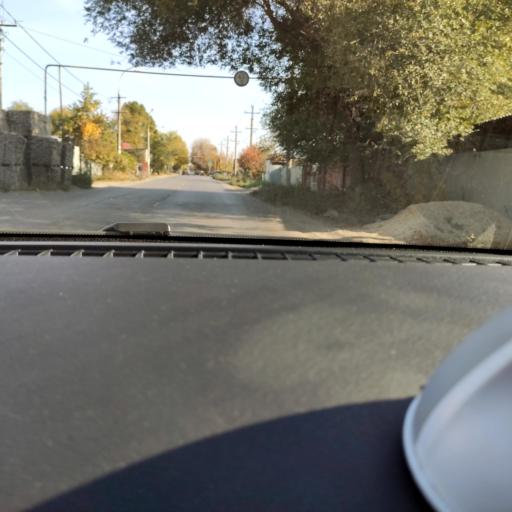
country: RU
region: Samara
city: Smyshlyayevka
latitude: 53.2357
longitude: 50.3214
